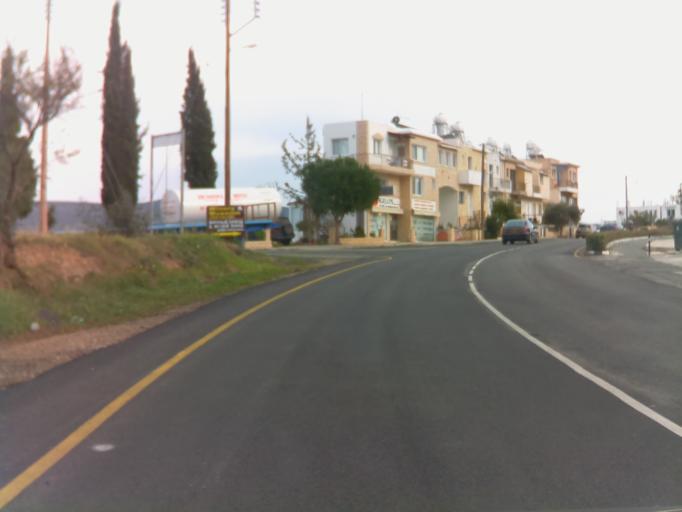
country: CY
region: Pafos
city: Polis
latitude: 35.0334
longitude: 32.4134
